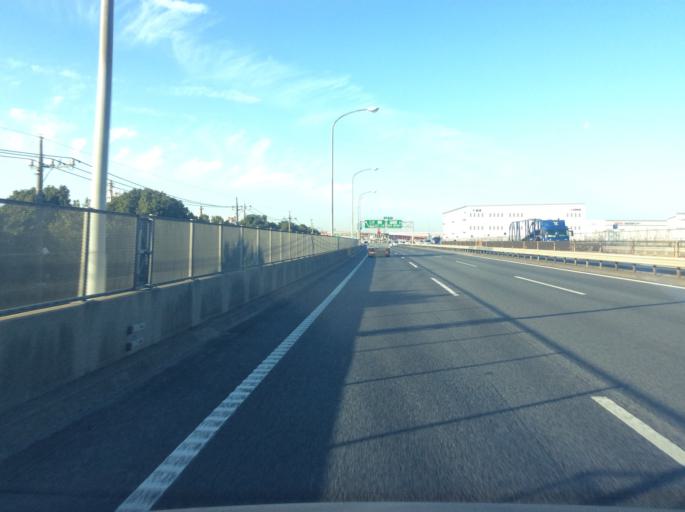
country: JP
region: Saitama
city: Yashio-shi
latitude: 35.8406
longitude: 139.8661
